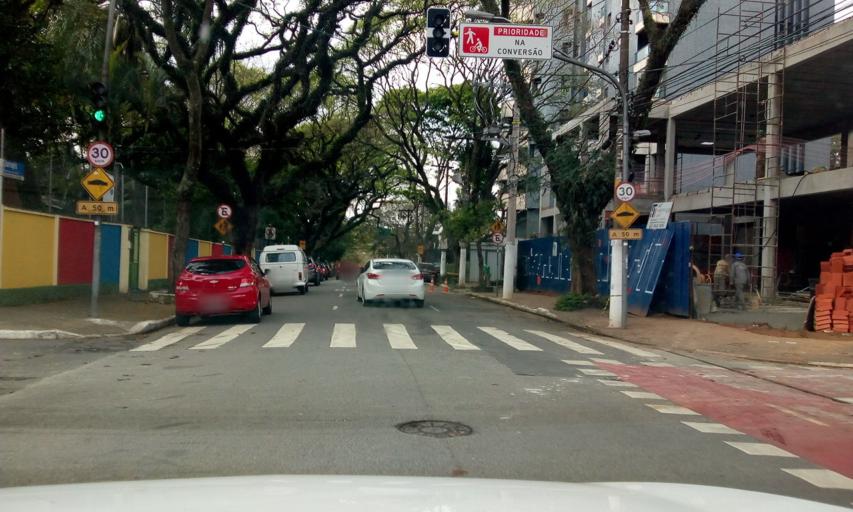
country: BR
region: Sao Paulo
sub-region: Sao Paulo
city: Sao Paulo
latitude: -23.6024
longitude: -46.6580
